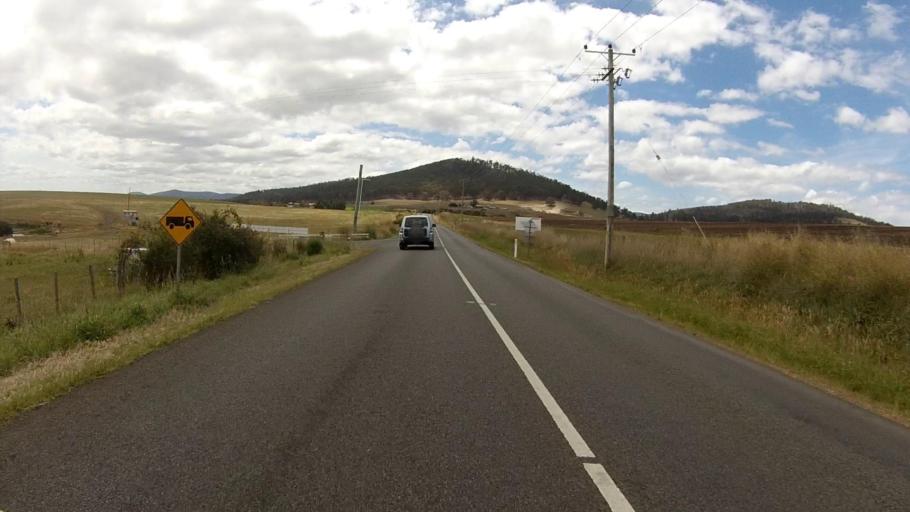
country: AU
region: Tasmania
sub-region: Sorell
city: Sorell
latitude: -42.8067
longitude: 147.6129
